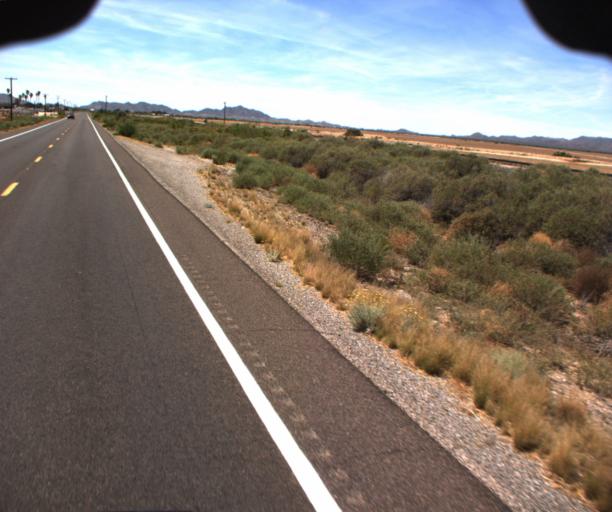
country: US
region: Arizona
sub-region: La Paz County
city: Salome
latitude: 33.7927
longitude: -113.5950
